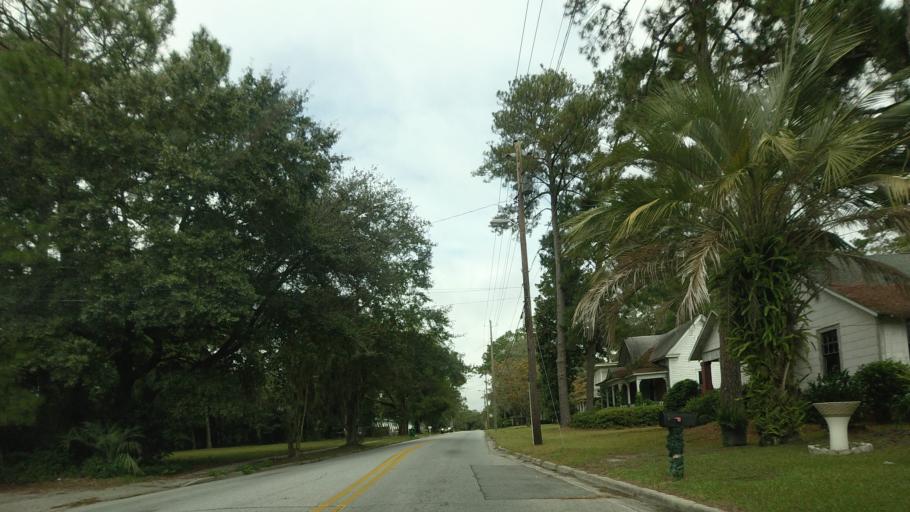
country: US
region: Georgia
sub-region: Lowndes County
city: Valdosta
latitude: 30.8387
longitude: -83.2861
